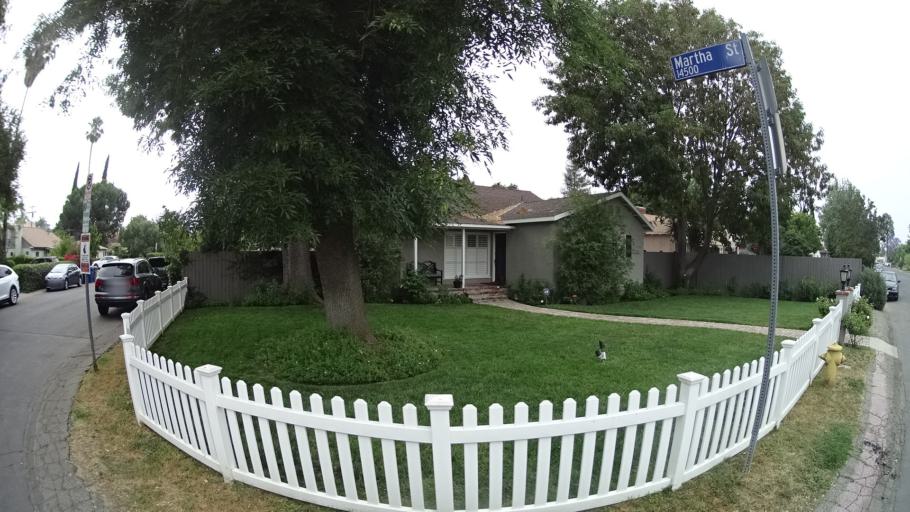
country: US
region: California
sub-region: Los Angeles County
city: Van Nuys
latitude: 34.1732
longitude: -118.4500
